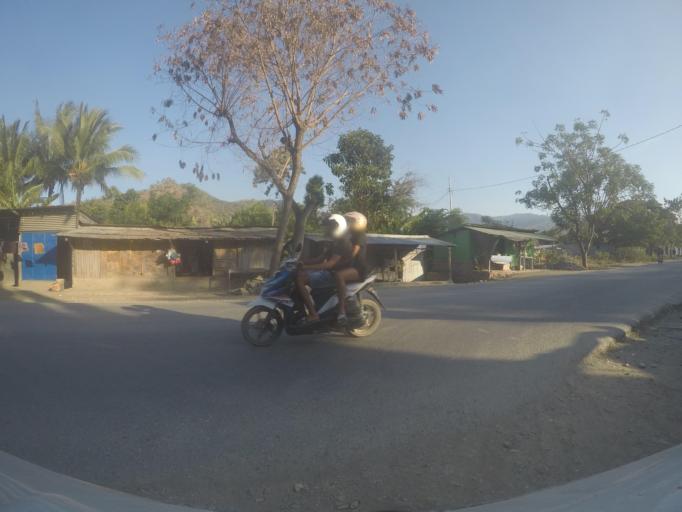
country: ID
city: Metinaro
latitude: -8.5479
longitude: 125.6666
